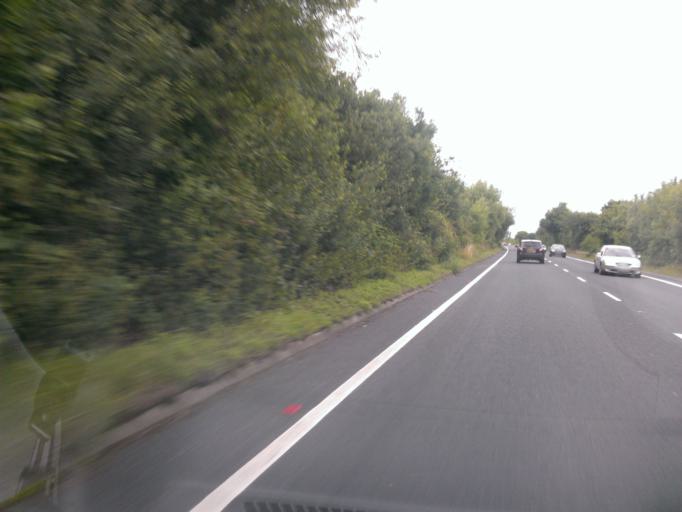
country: GB
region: England
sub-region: Essex
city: Little Clacton
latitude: 51.8283
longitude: 1.1310
